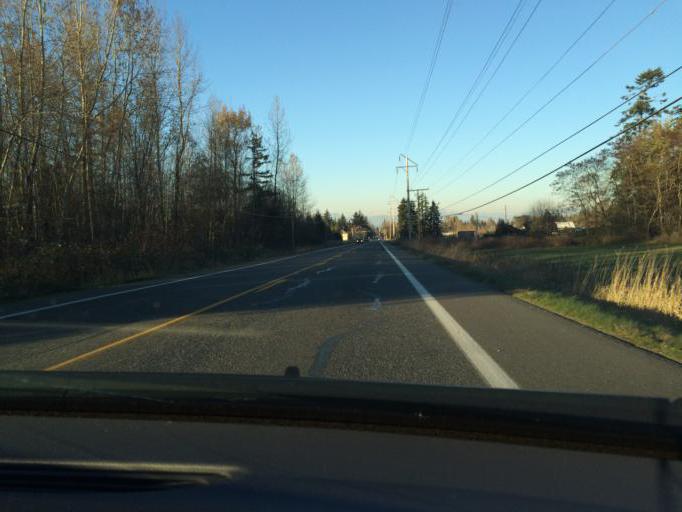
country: US
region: Washington
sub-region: Whatcom County
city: Bellingham
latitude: 48.8297
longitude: -122.4430
